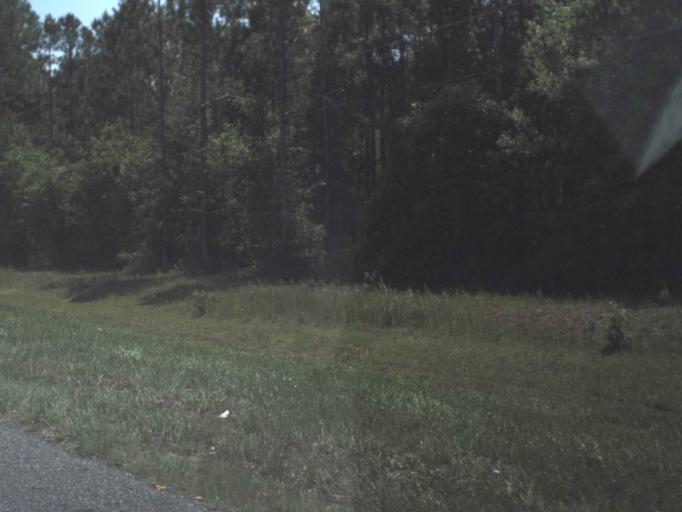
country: US
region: Florida
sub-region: Clay County
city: Green Cove Springs
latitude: 29.8215
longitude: -81.6607
